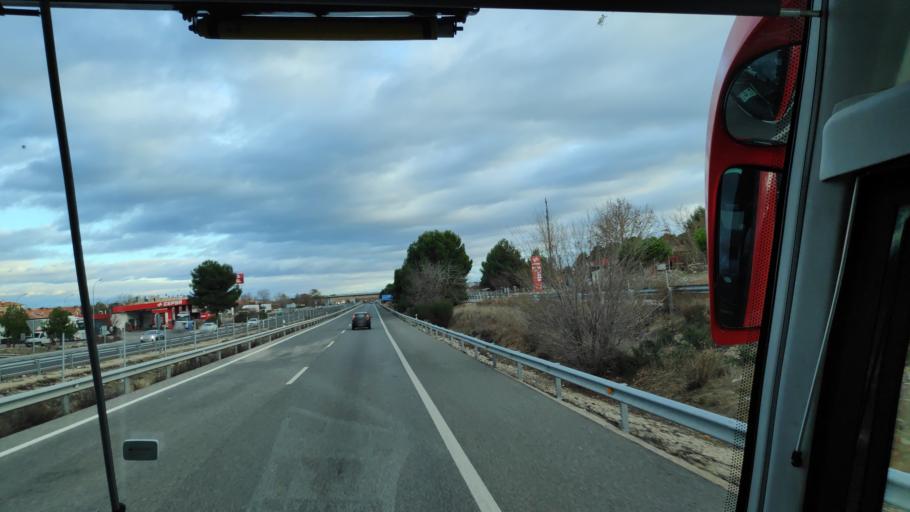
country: ES
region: Madrid
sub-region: Provincia de Madrid
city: Villarejo de Salvanes
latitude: 40.1681
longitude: -3.2873
